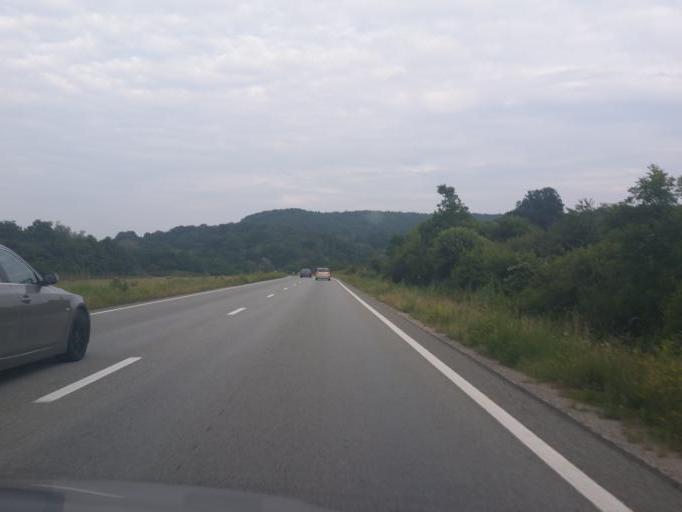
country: RO
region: Salaj
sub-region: Comuna Zimbor
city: Zimbor
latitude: 46.9654
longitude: 23.2909
